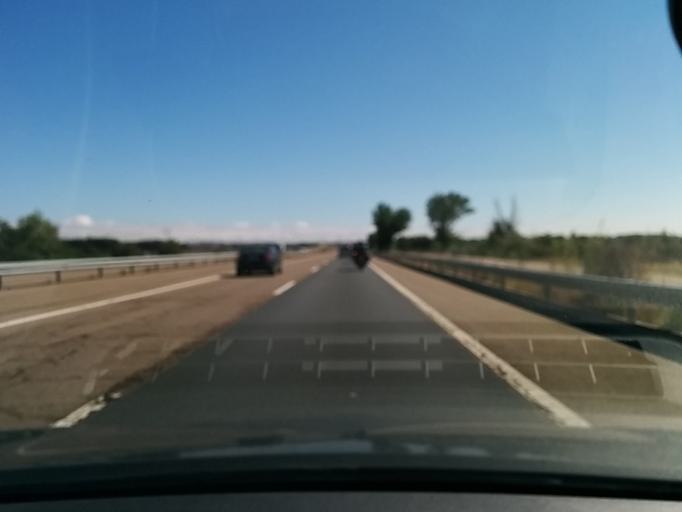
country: ES
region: Aragon
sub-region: Provincia de Huesca
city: Almudebar
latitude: 42.0292
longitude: -0.5932
